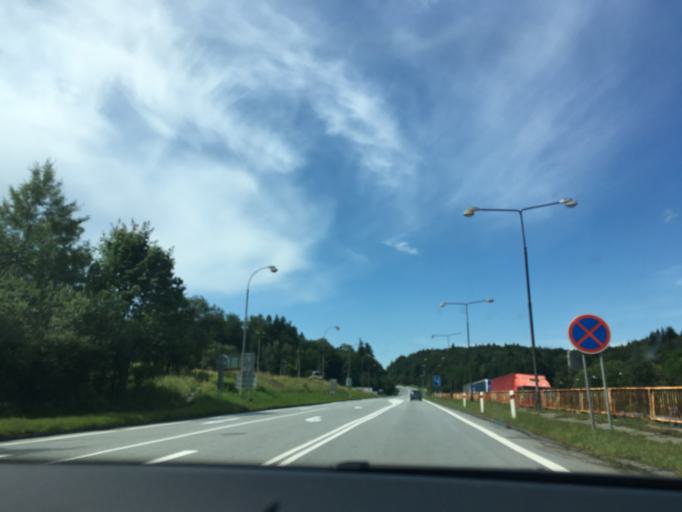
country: PL
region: Subcarpathian Voivodeship
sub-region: Powiat krosnienski
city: Jasliska
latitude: 49.4112
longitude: 21.7002
